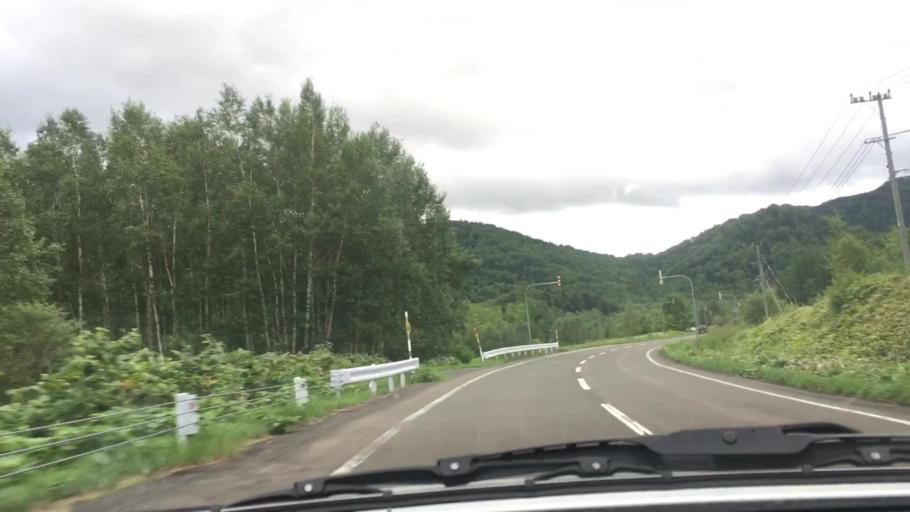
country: JP
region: Hokkaido
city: Shimo-furano
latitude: 43.0510
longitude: 142.5334
